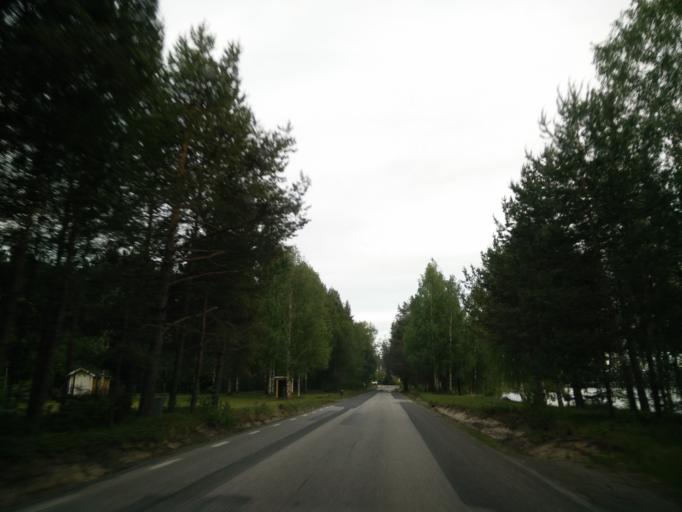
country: SE
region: Vaesternorrland
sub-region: Kramfors Kommun
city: Kramfors
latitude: 63.0294
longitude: 17.7890
